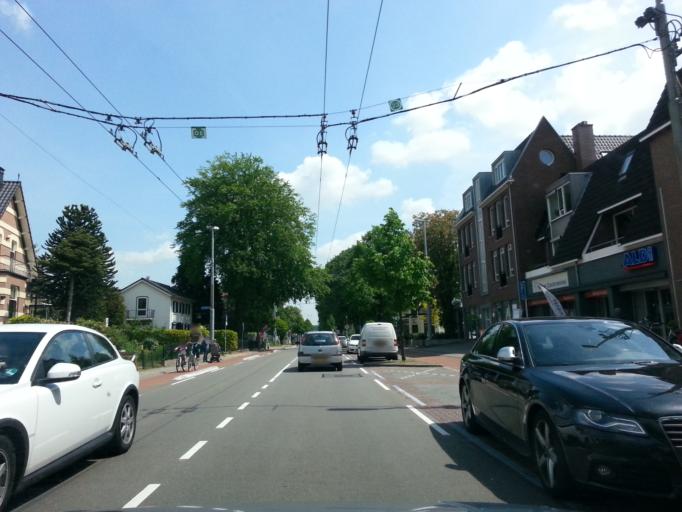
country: NL
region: Gelderland
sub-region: Gemeente Renkum
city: Oosterbeek
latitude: 51.9867
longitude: 5.8481
